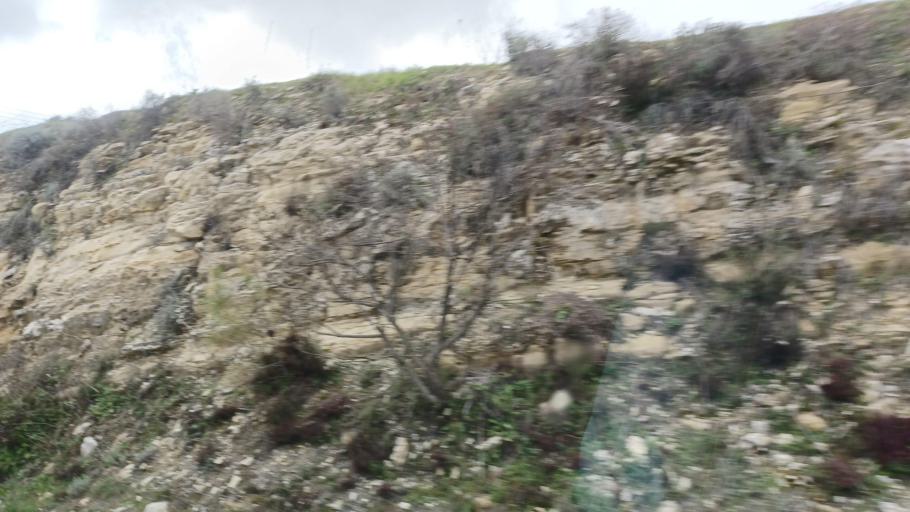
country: CY
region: Limassol
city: Pachna
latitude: 34.8374
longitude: 32.7710
